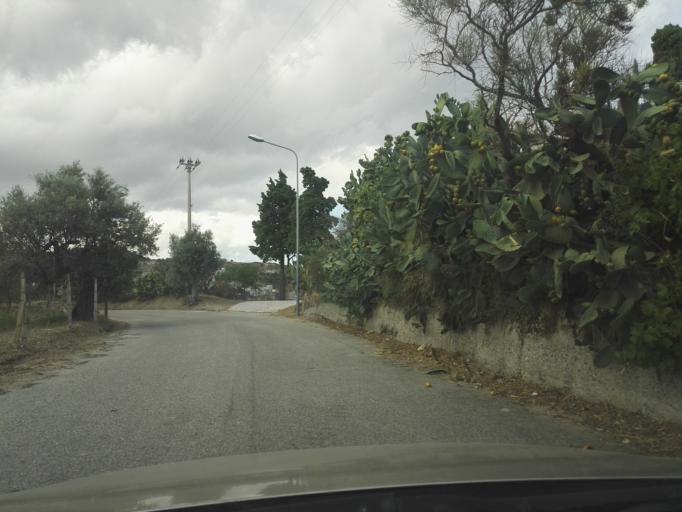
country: IT
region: Calabria
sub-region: Provincia di Reggio Calabria
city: Riace
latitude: 38.4147
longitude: 16.4829
